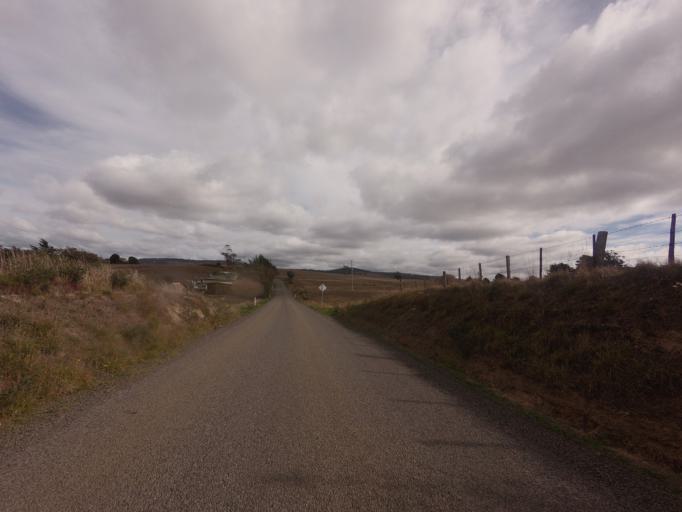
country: AU
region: Tasmania
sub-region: Brighton
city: Bridgewater
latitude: -42.4295
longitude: 147.3876
